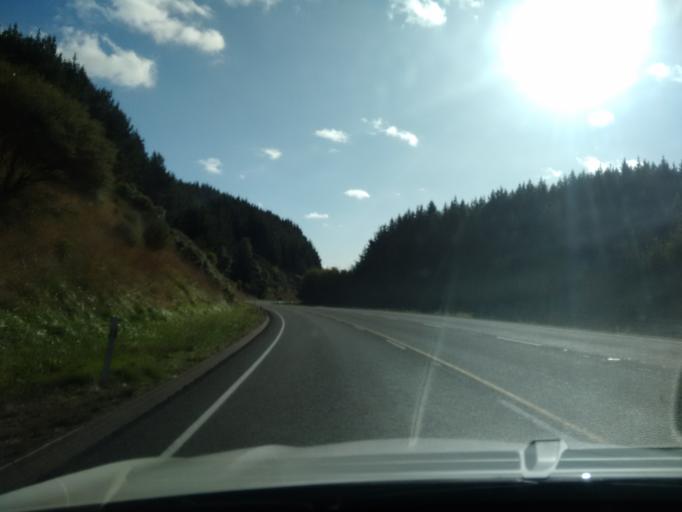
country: NZ
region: Manawatu-Wanganui
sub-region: Wanganui District
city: Wanganui
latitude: -39.8325
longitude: 174.9028
